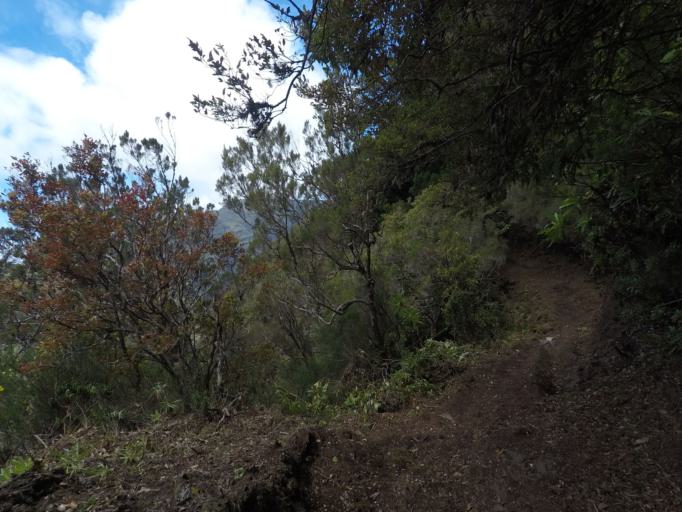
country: PT
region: Madeira
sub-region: Camara de Lobos
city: Curral das Freiras
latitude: 32.7579
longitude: -16.9747
